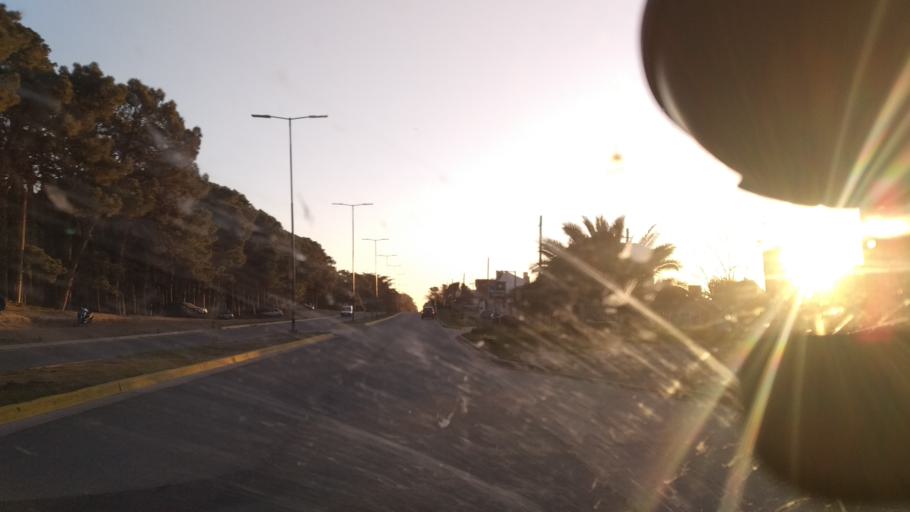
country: AR
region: Buenos Aires
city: Necochea
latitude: -38.5830
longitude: -58.7443
